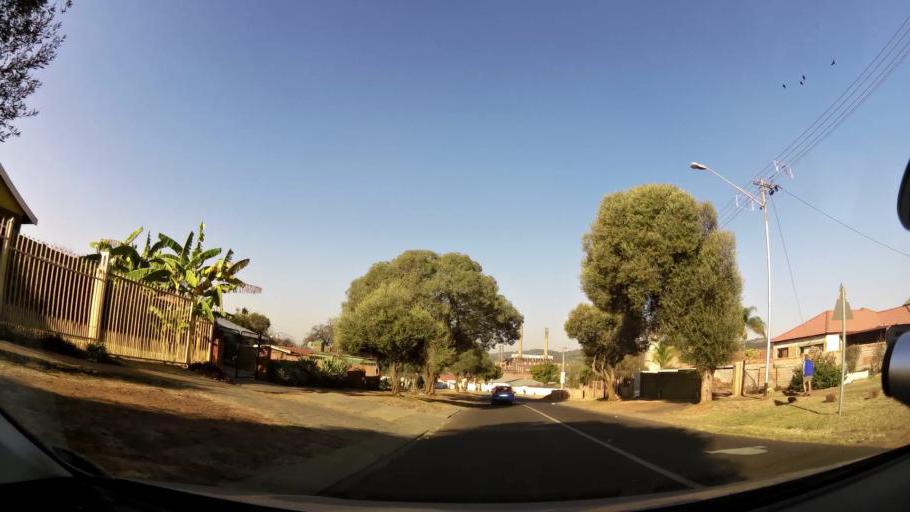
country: ZA
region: Gauteng
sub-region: City of Tshwane Metropolitan Municipality
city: Pretoria
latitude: -25.7547
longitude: 28.1397
